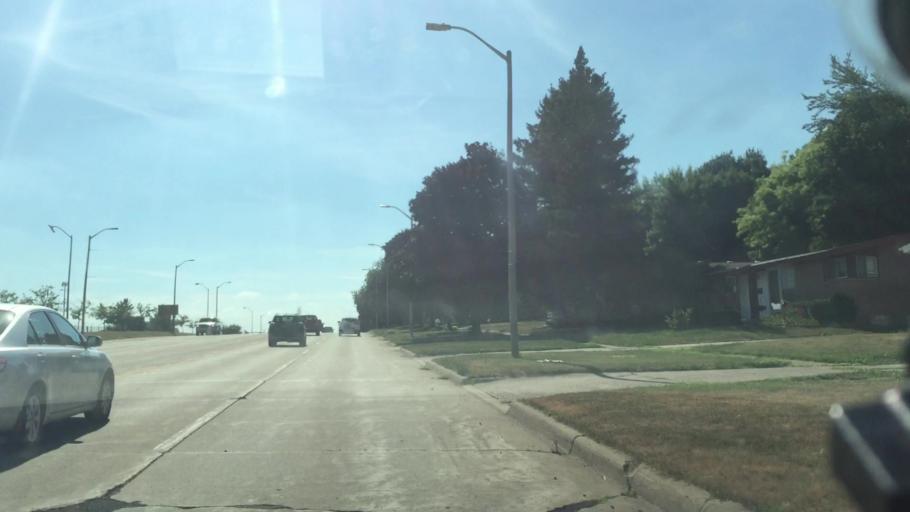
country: US
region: Michigan
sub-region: Oakland County
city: Pontiac
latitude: 42.6492
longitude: -83.2516
